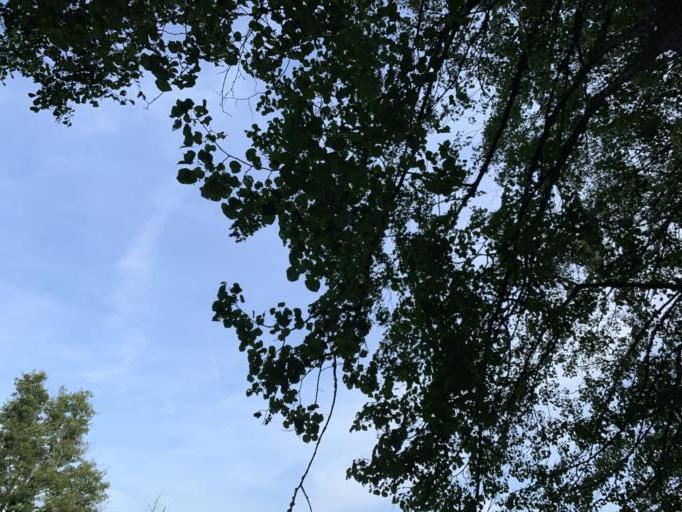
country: SE
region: Vaestmanland
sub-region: Hallstahammars Kommun
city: Kolback
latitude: 59.4739
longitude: 16.2169
